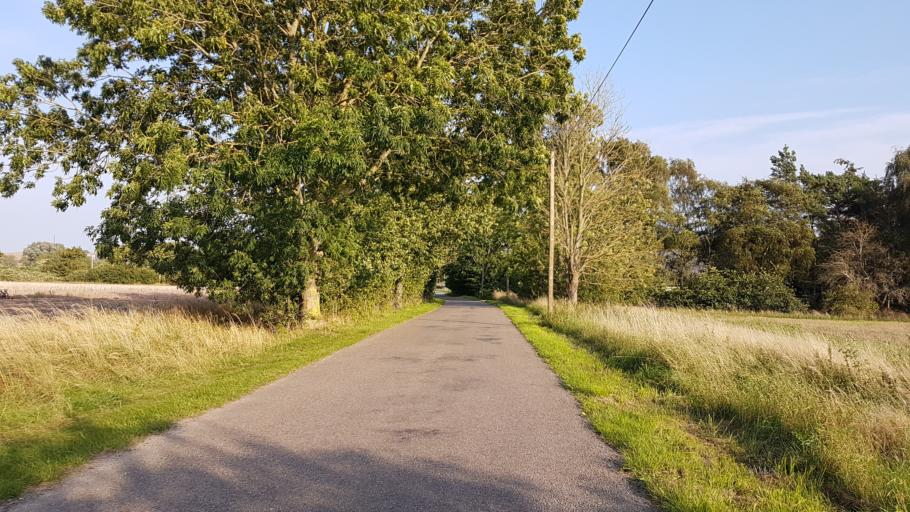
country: DE
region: Mecklenburg-Vorpommern
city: Sagard
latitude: 54.5043
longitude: 13.5272
